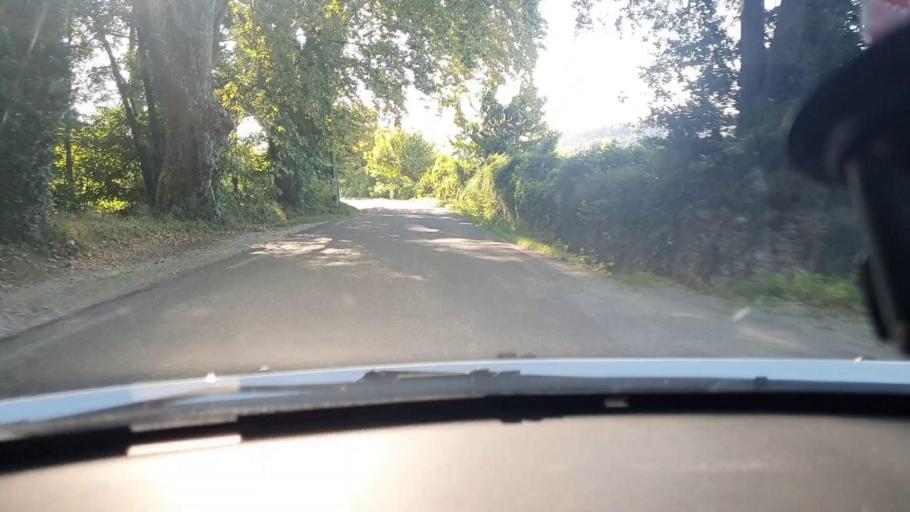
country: FR
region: Languedoc-Roussillon
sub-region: Departement du Gard
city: Goudargues
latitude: 44.2035
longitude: 4.4691
